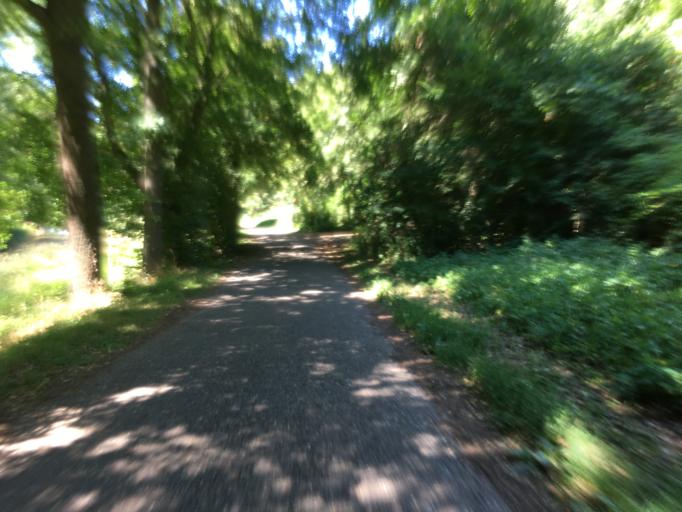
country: DE
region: Baden-Wuerttemberg
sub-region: Karlsruhe Region
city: Illingen
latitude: 48.9451
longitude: 8.9047
